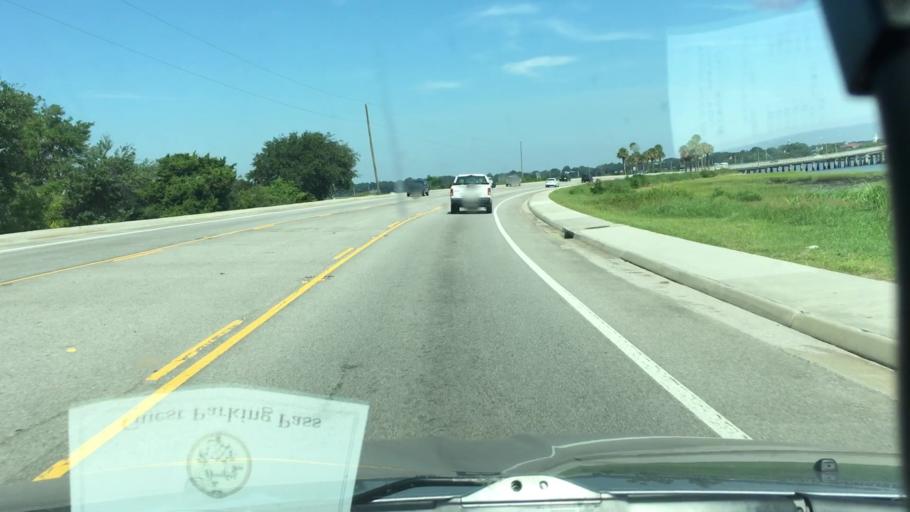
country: US
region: South Carolina
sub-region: Beaufort County
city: Beaufort
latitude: 32.4218
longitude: -80.6659
